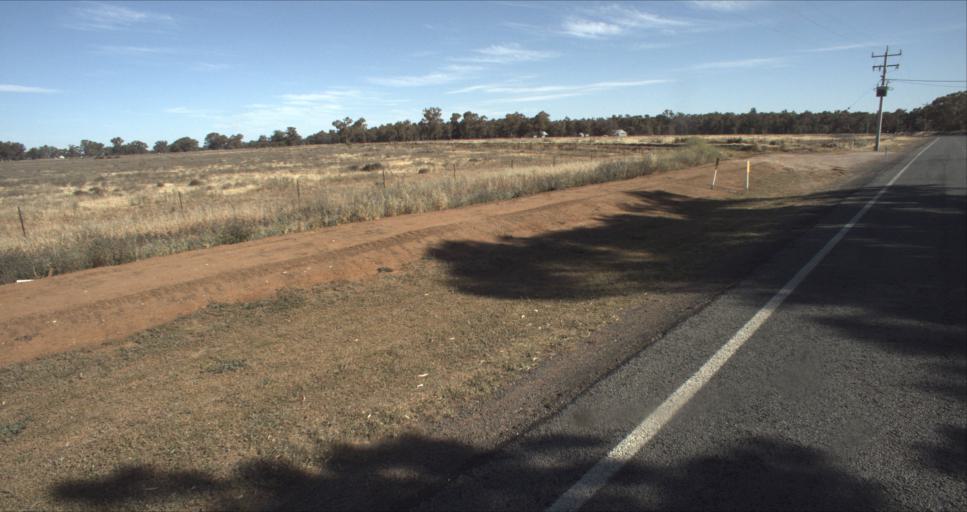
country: AU
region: New South Wales
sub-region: Leeton
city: Leeton
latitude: -34.6208
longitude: 146.3972
